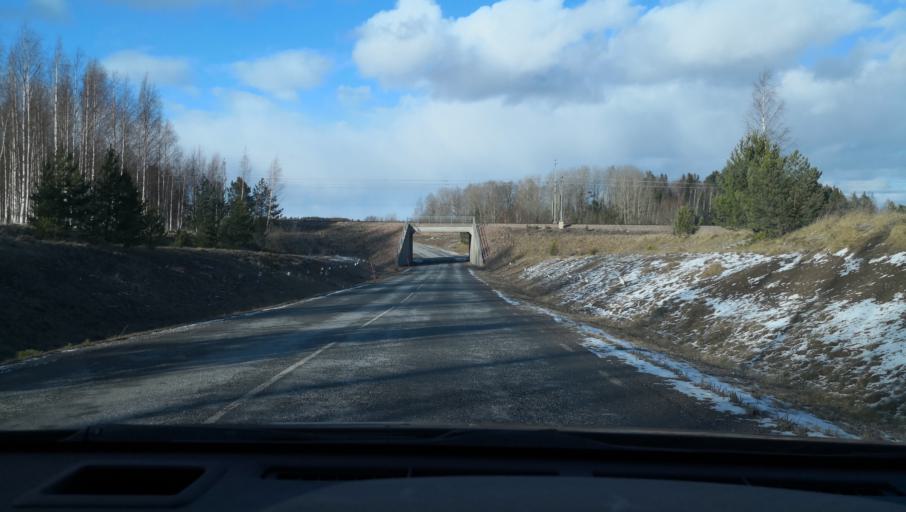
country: SE
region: Uppsala
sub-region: Enkopings Kommun
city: Hummelsta
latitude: 59.6506
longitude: 16.9643
